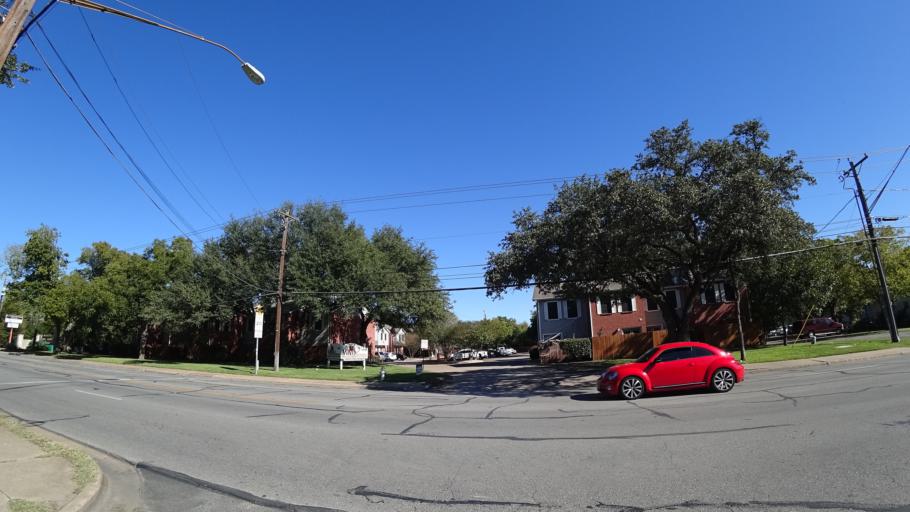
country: US
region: Texas
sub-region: Travis County
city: Rollingwood
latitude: 30.2329
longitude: -97.7864
